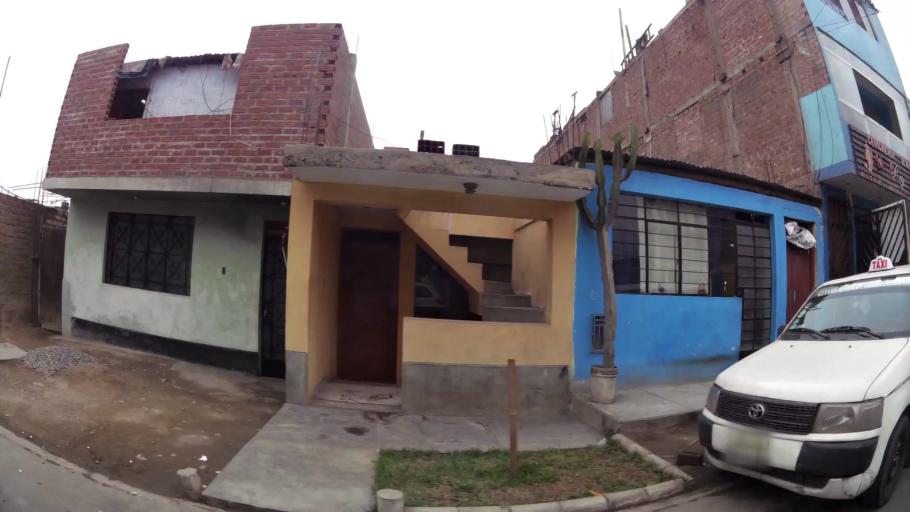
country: PE
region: Lima
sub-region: Lima
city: Urb. Santo Domingo
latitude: -11.9391
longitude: -76.9710
